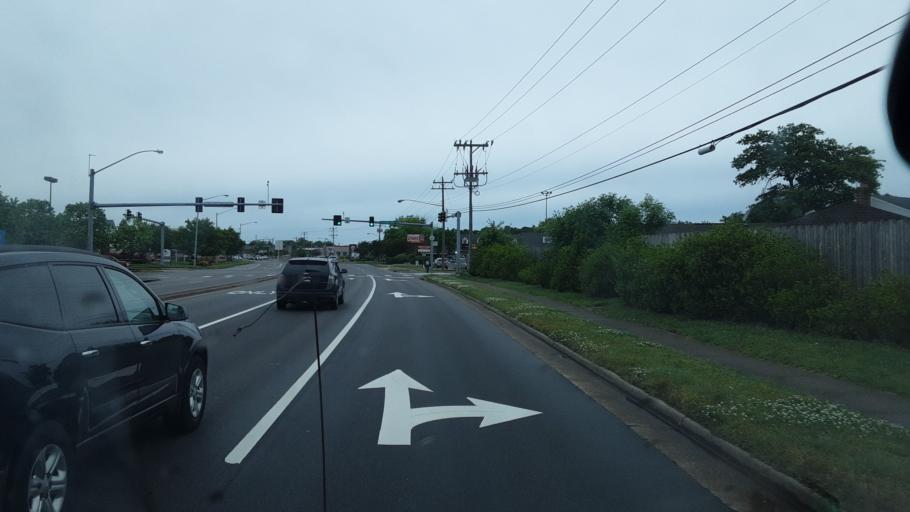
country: US
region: Virginia
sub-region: City of Virginia Beach
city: Virginia Beach
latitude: 36.8160
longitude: -76.1073
